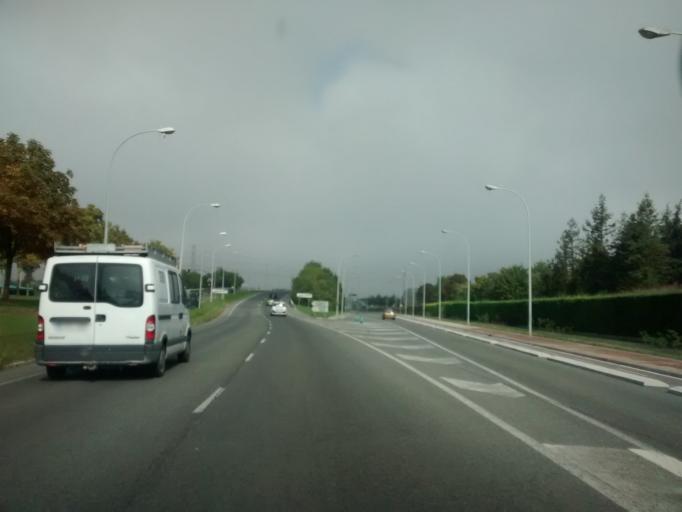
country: ES
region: Basque Country
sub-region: Provincia de Alava
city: Gasteiz / Vitoria
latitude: 42.8708
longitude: -2.6893
